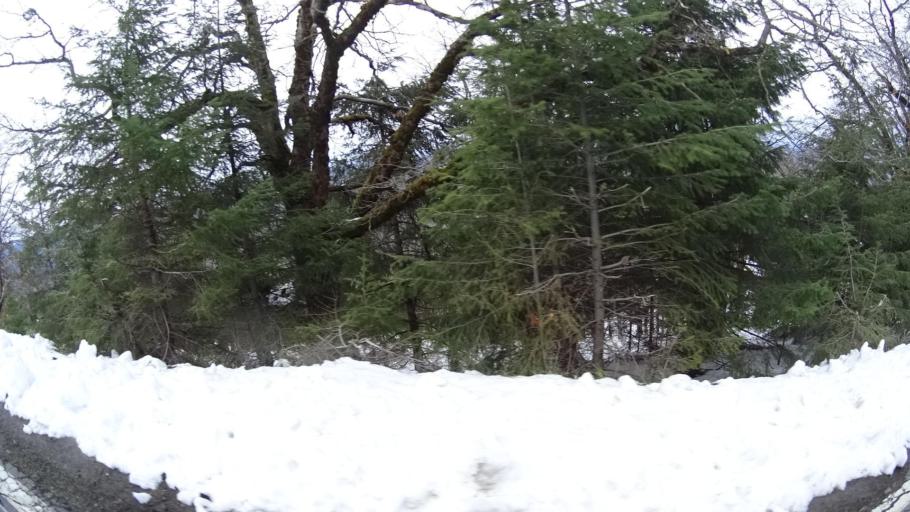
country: US
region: California
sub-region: Humboldt County
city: Willow Creek
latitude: 40.8714
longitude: -123.7529
